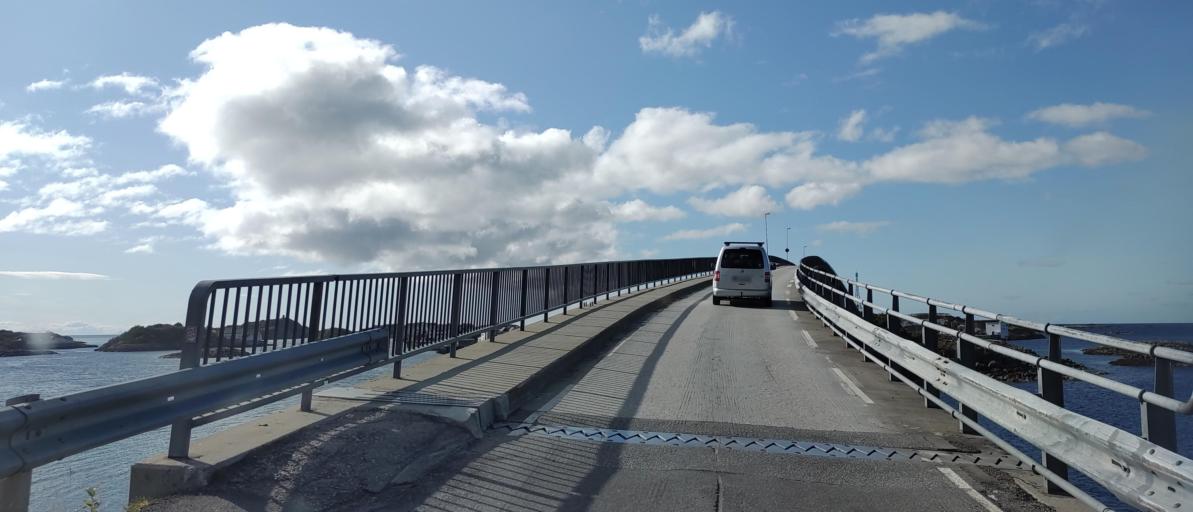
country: NO
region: Nordland
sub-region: Vagan
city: Kabelvag
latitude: 68.1597
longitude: 14.2150
